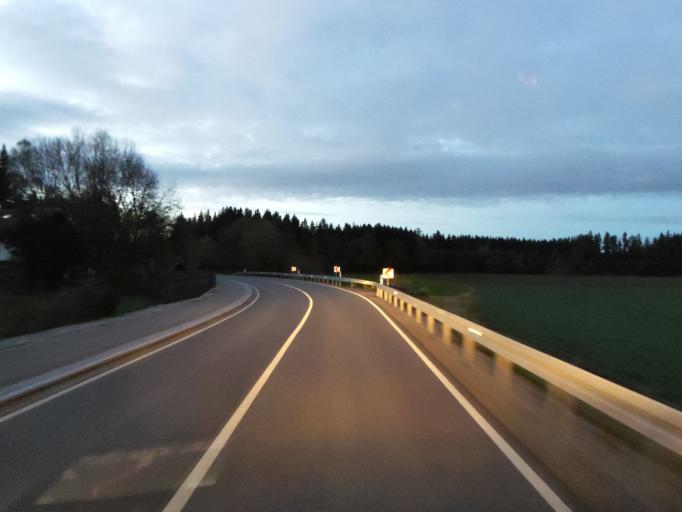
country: DE
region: Bavaria
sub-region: Upper Bavaria
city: Hohenkirchen-Siegertsbrunn
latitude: 47.9933
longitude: 11.7115
